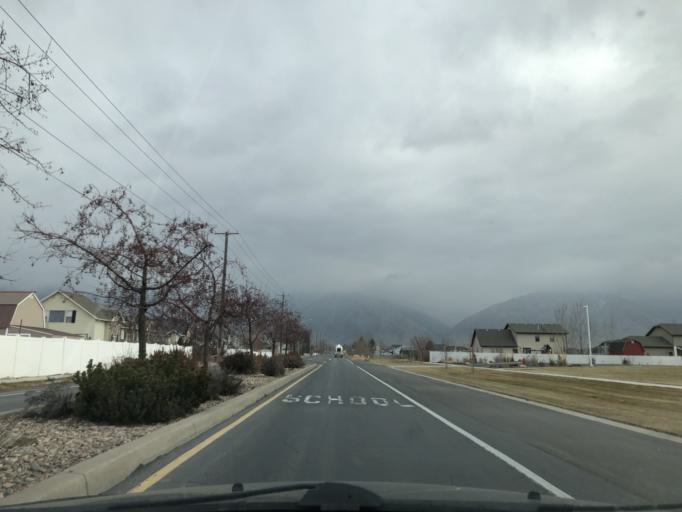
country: US
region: Utah
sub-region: Cache County
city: Nibley
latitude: 41.6752
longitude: -111.8705
